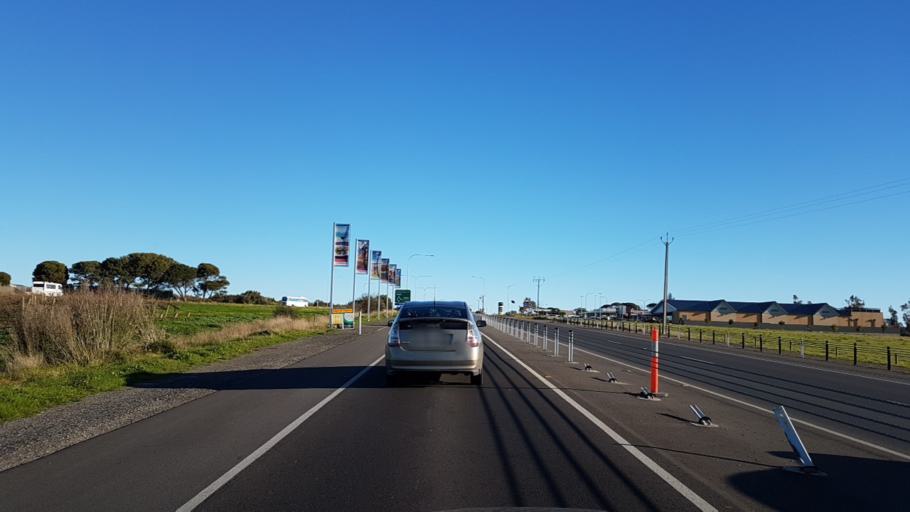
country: AU
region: South Australia
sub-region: Onkaparinga
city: Aldinga
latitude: -35.2656
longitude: 138.4866
